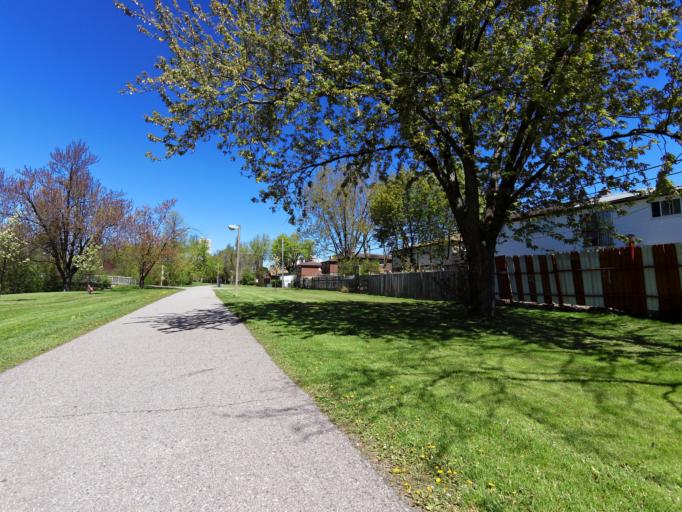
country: CA
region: Ontario
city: Brampton
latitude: 43.7143
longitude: -79.7098
